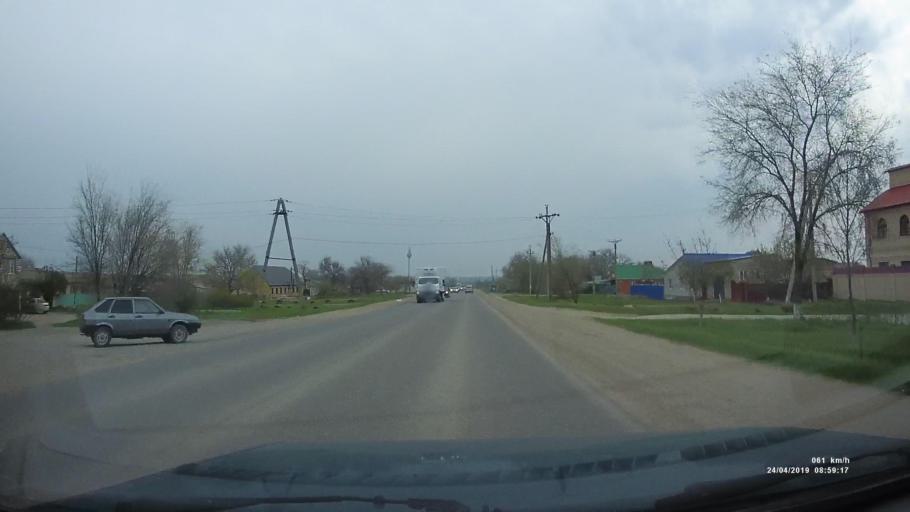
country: RU
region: Kalmykiya
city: Arshan'
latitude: 46.3123
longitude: 44.2077
